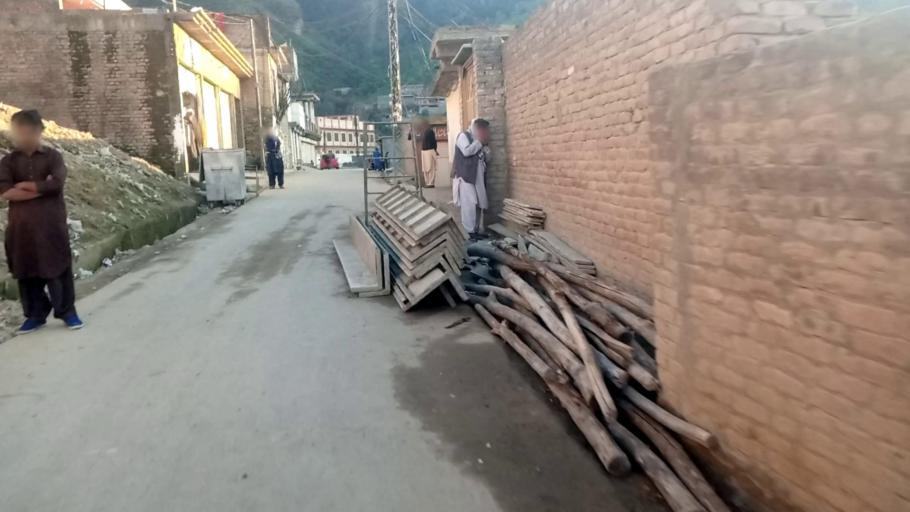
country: PK
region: Khyber Pakhtunkhwa
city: Saidu Sharif
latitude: 34.7378
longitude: 72.3448
